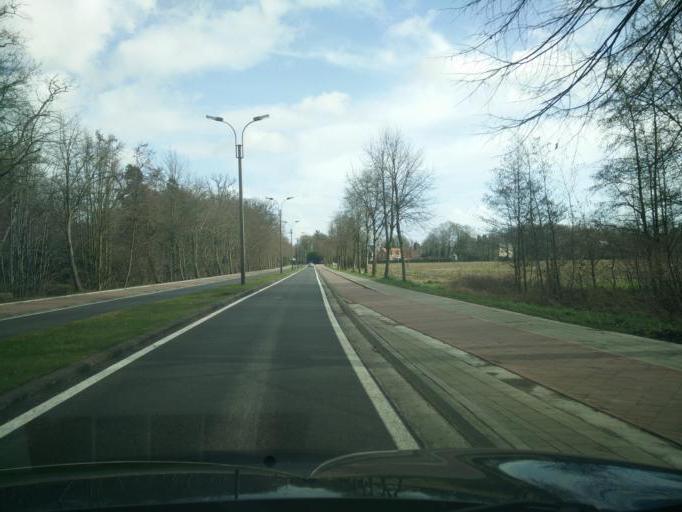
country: BE
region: Flanders
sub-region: Provincie Oost-Vlaanderen
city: Melle
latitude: 51.0282
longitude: 3.7920
